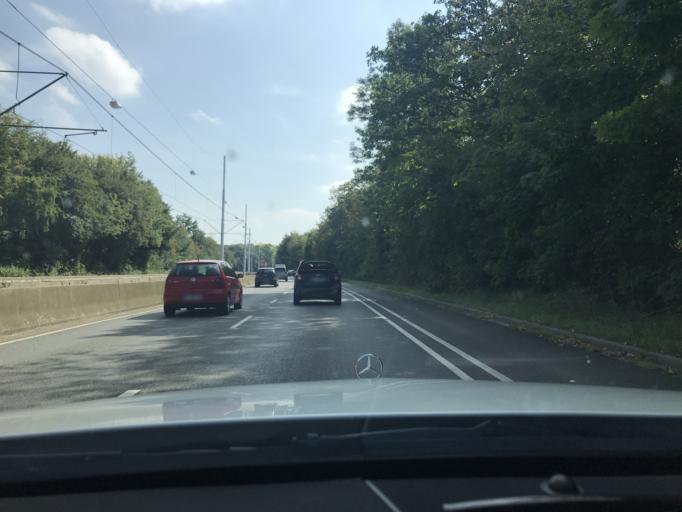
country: DE
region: North Rhine-Westphalia
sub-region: Regierungsbezirk Arnsberg
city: Bochum
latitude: 51.4558
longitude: 7.2406
